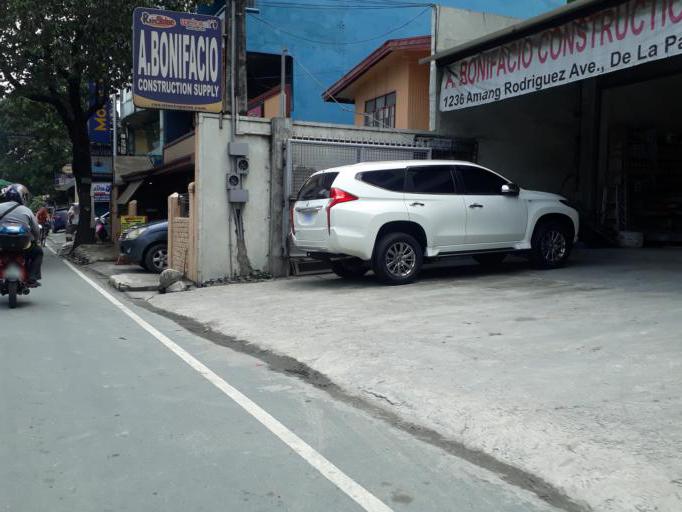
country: PH
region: Metro Manila
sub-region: Marikina
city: Calumpang
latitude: 14.6132
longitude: 121.0923
